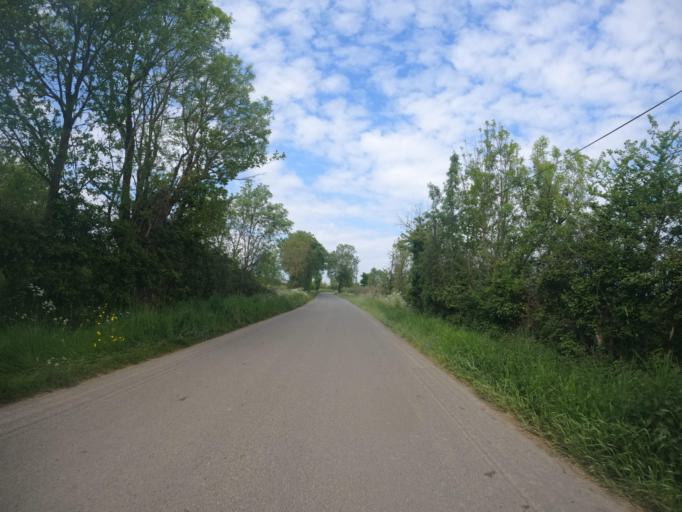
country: FR
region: Poitou-Charentes
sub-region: Departement des Deux-Sevres
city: Saint-Varent
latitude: 46.8887
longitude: -0.2908
